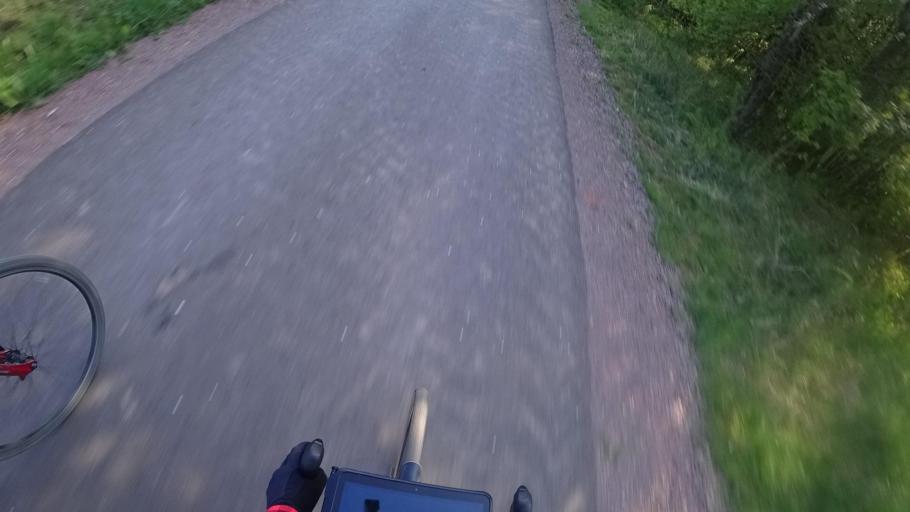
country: DE
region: Rheinland-Pfalz
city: Ayl
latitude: 49.6254
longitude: 6.5406
